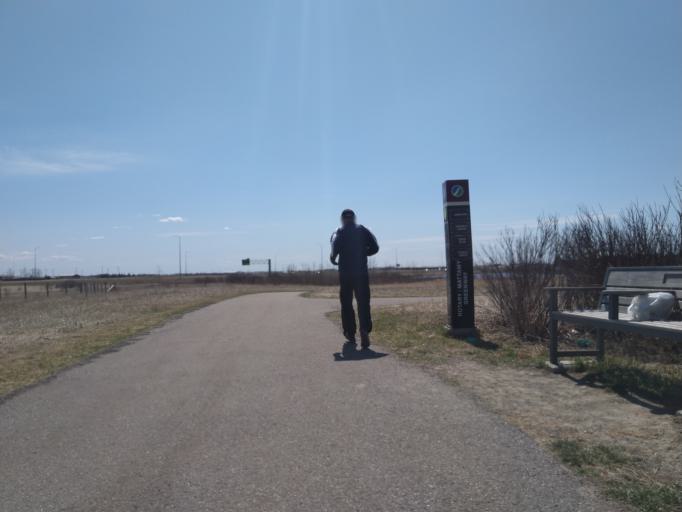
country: CA
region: Alberta
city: Chestermere
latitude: 51.0866
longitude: -113.9233
